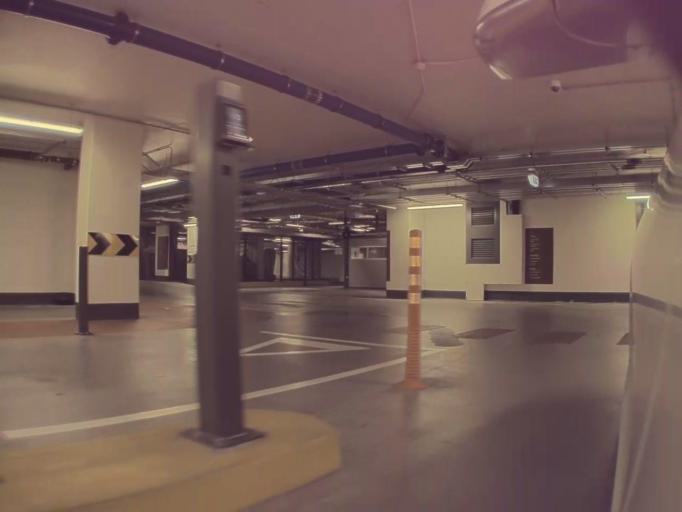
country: IE
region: Leinster
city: Ringsend
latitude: 53.3449
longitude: -6.2322
